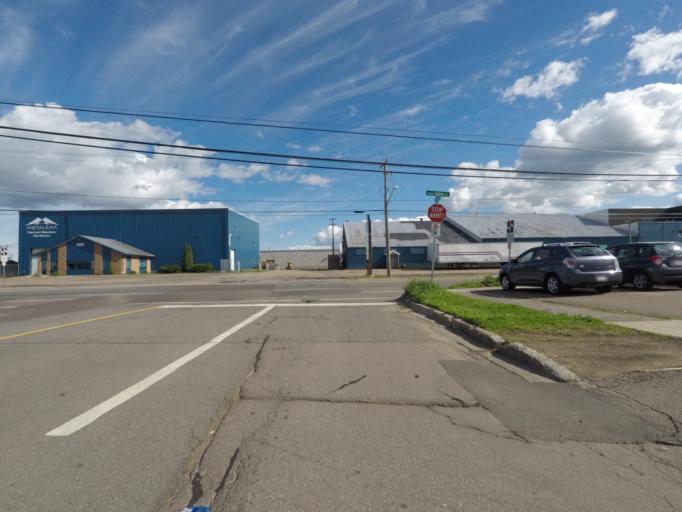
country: CA
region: New Brunswick
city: Moncton
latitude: 46.0952
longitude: -64.8265
